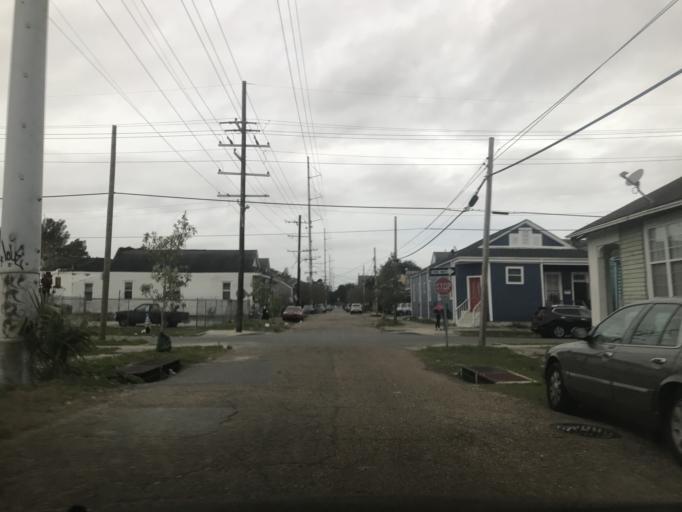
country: US
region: Louisiana
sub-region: Orleans Parish
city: New Orleans
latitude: 29.9650
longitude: -90.0949
